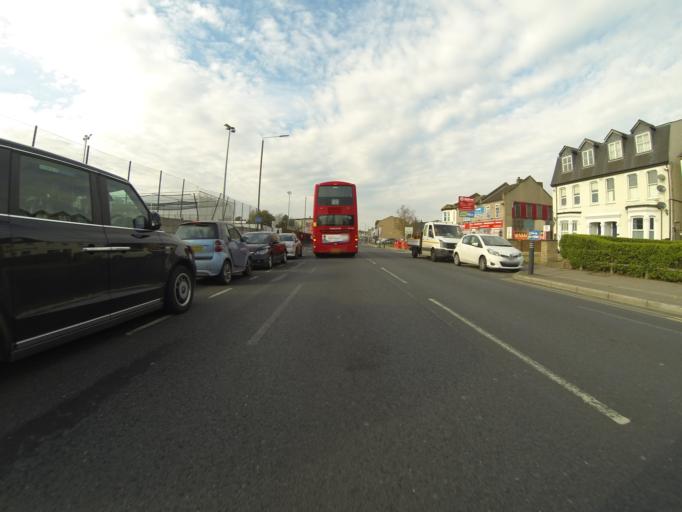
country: GB
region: England
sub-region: Greater London
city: Welling
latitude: 51.4607
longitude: 0.1181
